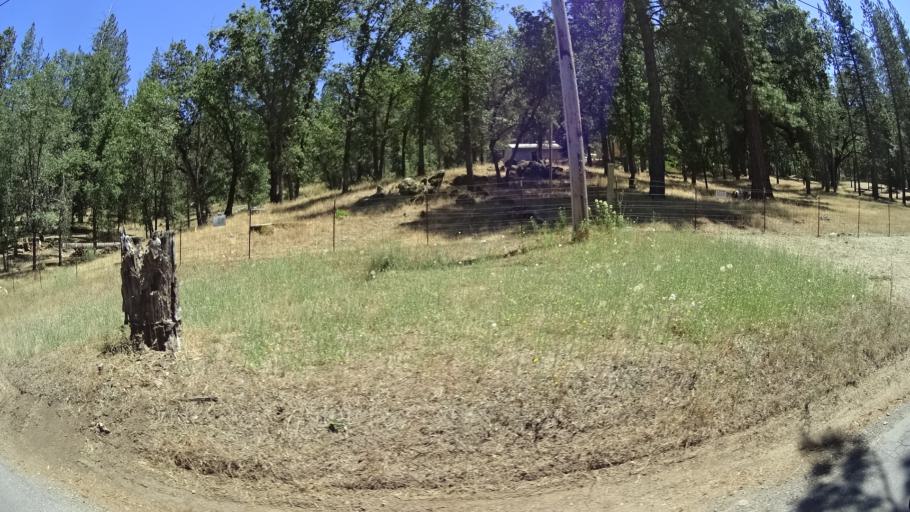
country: US
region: California
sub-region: Calaveras County
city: Mountain Ranch
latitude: 38.2679
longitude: -120.4977
